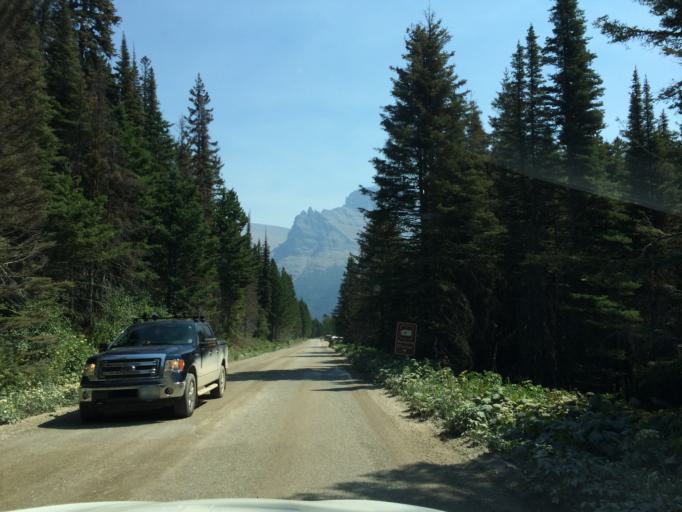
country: US
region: Montana
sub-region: Flathead County
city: Columbia Falls
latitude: 48.6795
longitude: -113.6563
